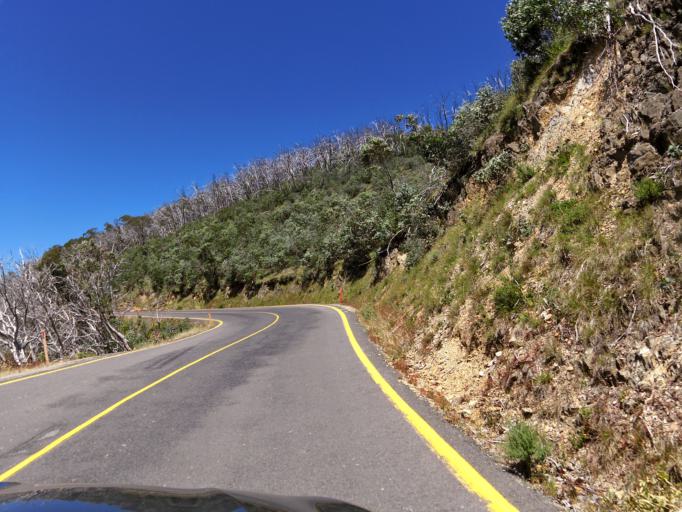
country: AU
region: Victoria
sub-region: Alpine
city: Mount Beauty
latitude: -37.0065
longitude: 147.0768
